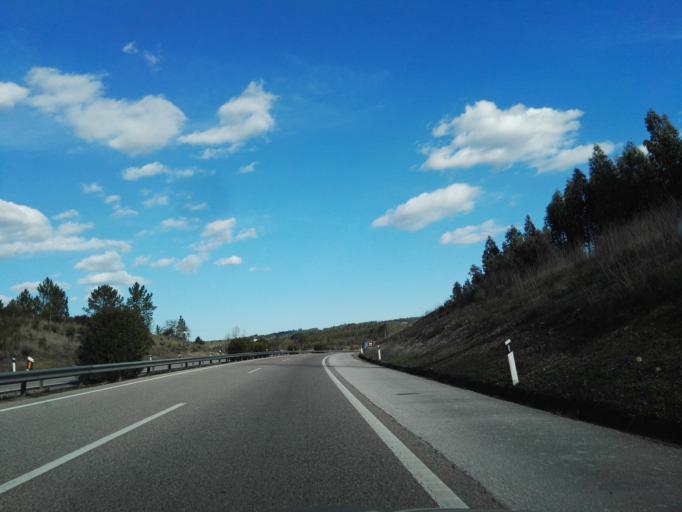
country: PT
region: Santarem
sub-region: Entroncamento
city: Entroncamento
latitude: 39.4891
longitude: -8.4597
